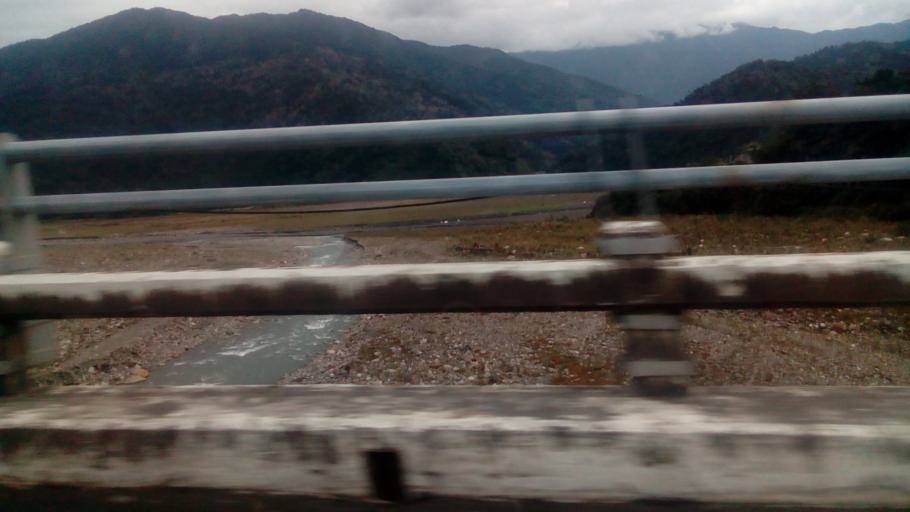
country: TW
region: Taiwan
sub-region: Yilan
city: Yilan
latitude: 24.5785
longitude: 121.4932
